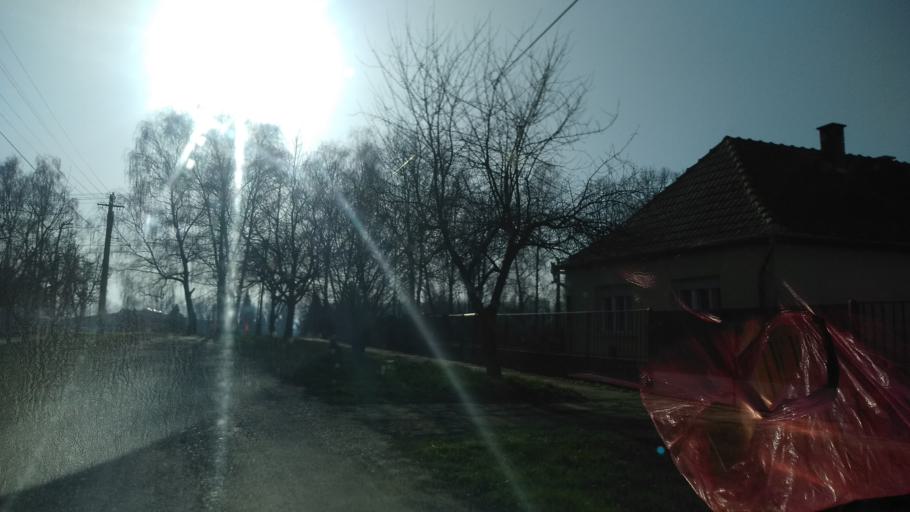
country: HU
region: Somogy
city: Barcs
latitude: 45.9630
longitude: 17.4892
